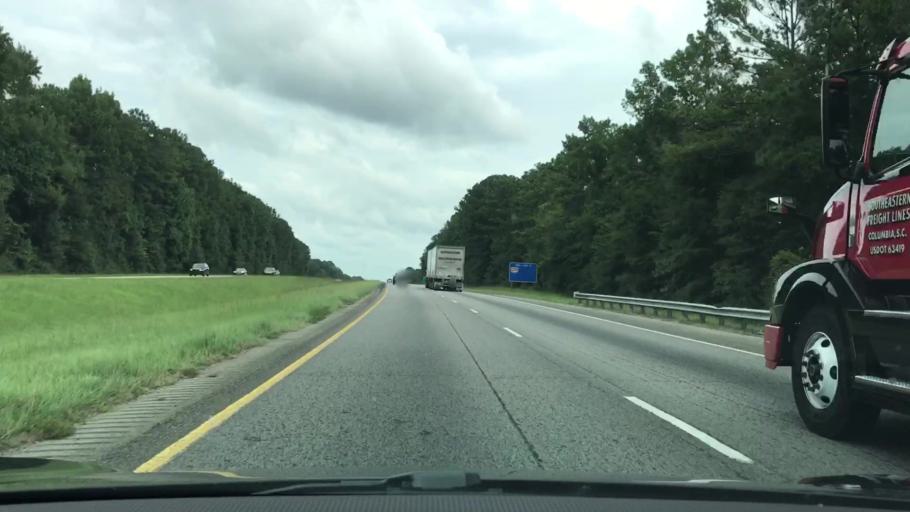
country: US
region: Georgia
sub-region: Troup County
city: La Grange
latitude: 32.9831
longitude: -85.0378
